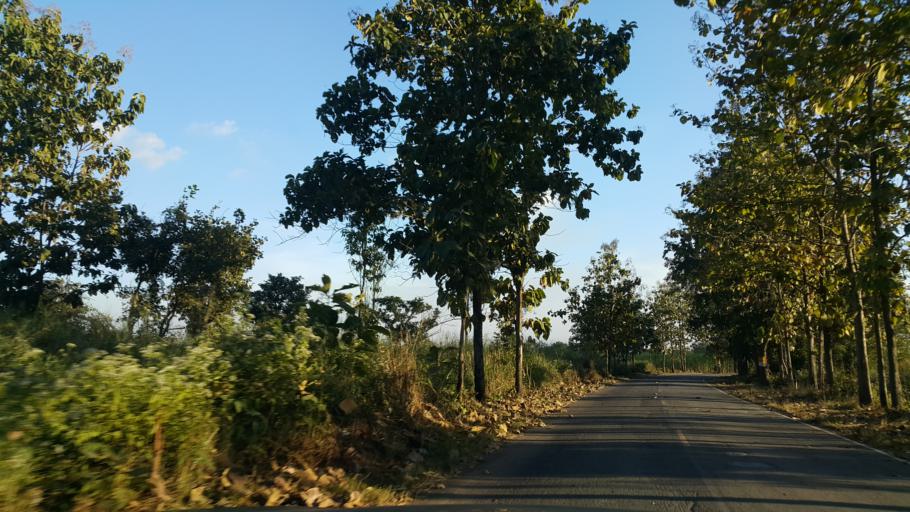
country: TH
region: Sukhothai
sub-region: Amphoe Si Satchanalai
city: Si Satchanalai
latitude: 17.5497
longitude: 99.9034
